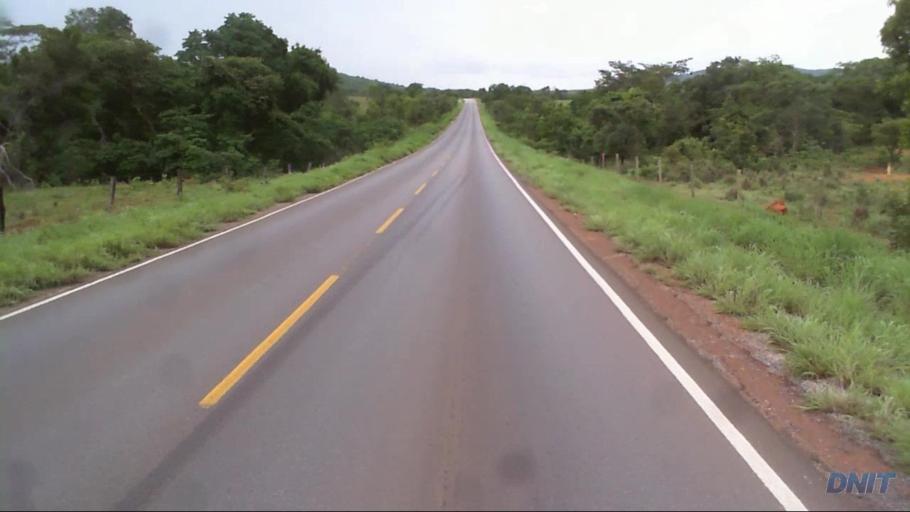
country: BR
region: Goias
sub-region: Padre Bernardo
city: Padre Bernardo
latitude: -15.4422
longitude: -48.1981
